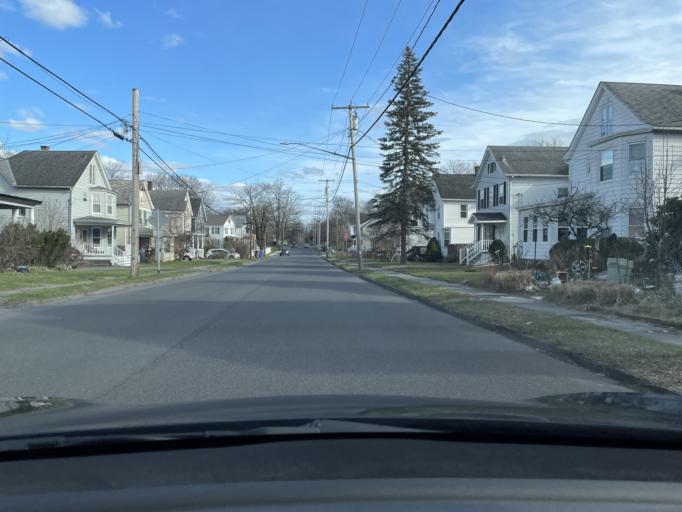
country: US
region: New York
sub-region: Ulster County
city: Kingston
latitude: 41.9253
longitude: -74.0159
